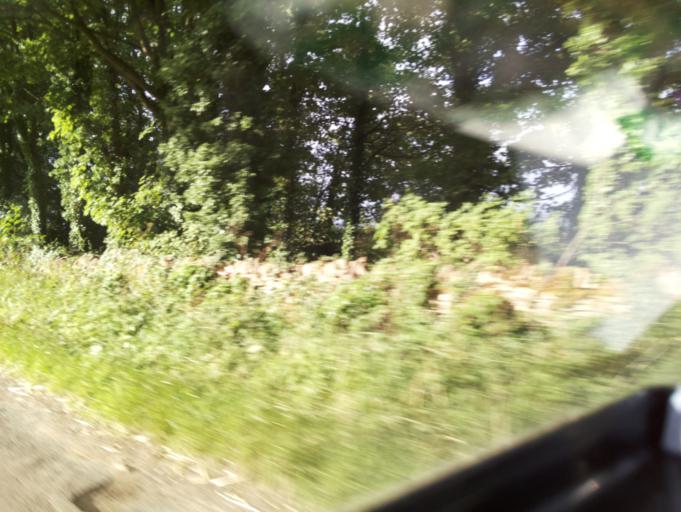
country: GB
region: England
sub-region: Gloucestershire
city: Donnington
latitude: 51.9720
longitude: -1.7519
